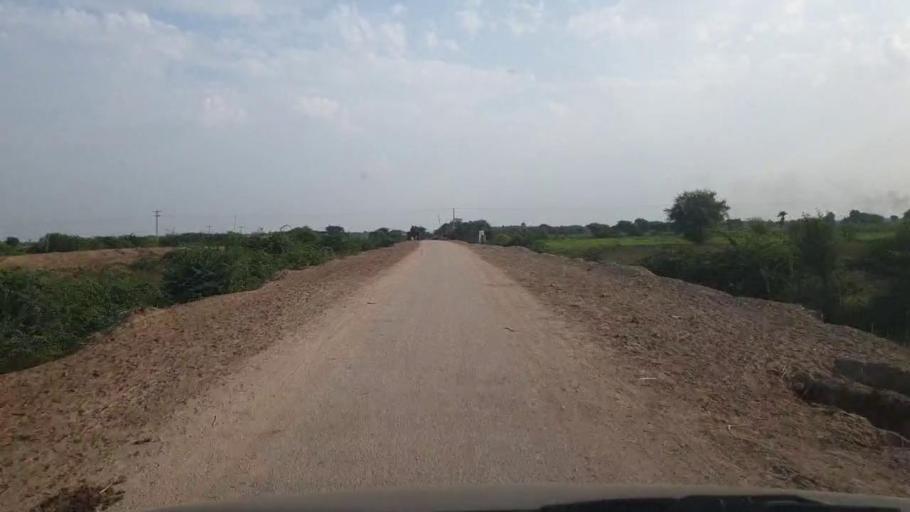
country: PK
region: Sindh
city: Badin
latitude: 24.5306
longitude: 68.6782
